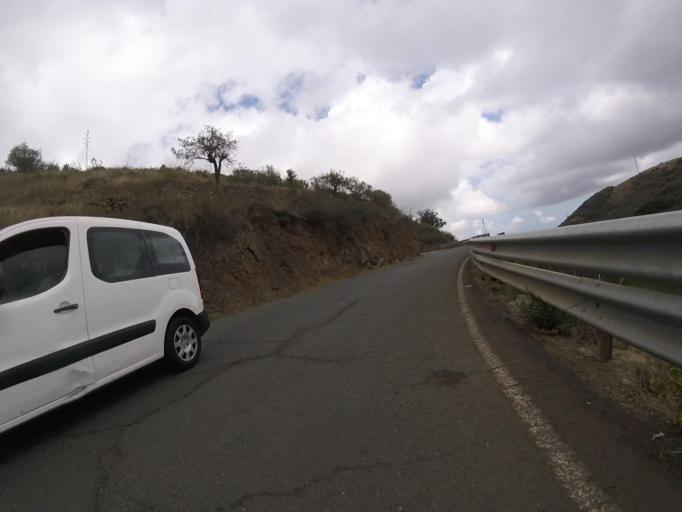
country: ES
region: Canary Islands
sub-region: Provincia de Las Palmas
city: Vega de San Mateo
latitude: 27.9950
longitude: -15.5685
